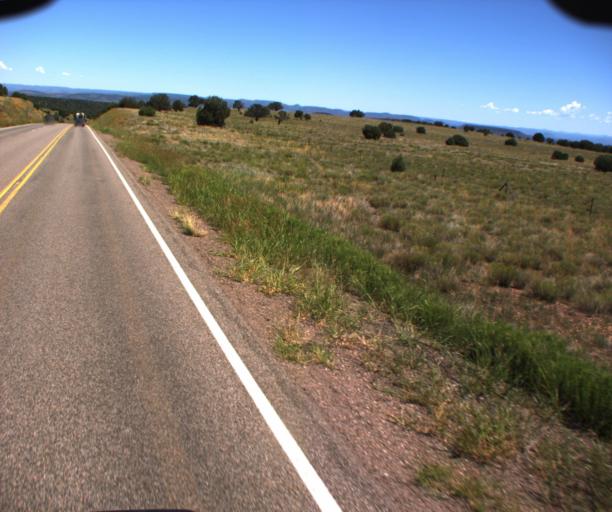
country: US
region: Arizona
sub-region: Navajo County
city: Cibecue
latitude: 33.7195
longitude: -110.5326
